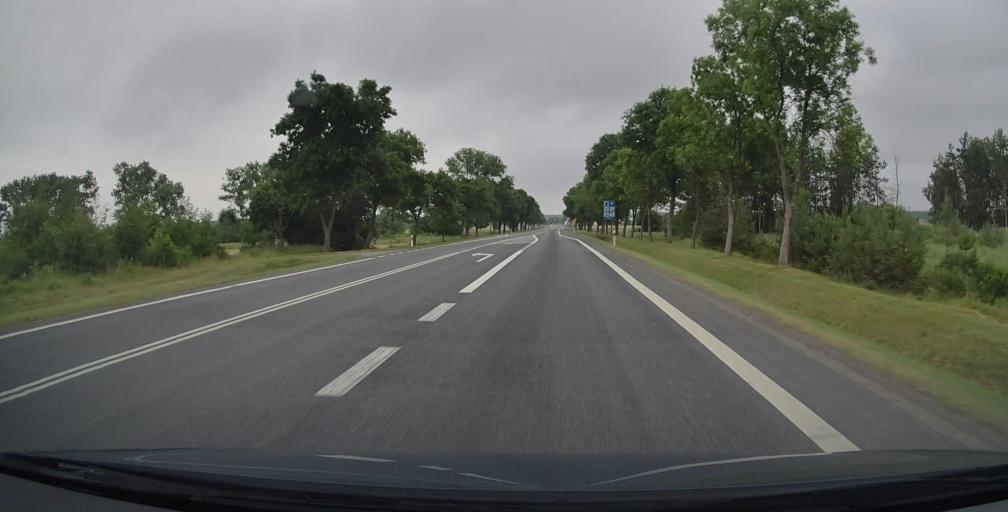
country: PL
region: Lublin Voivodeship
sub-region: Powiat bialski
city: Rokitno
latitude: 52.0348
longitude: 23.2587
